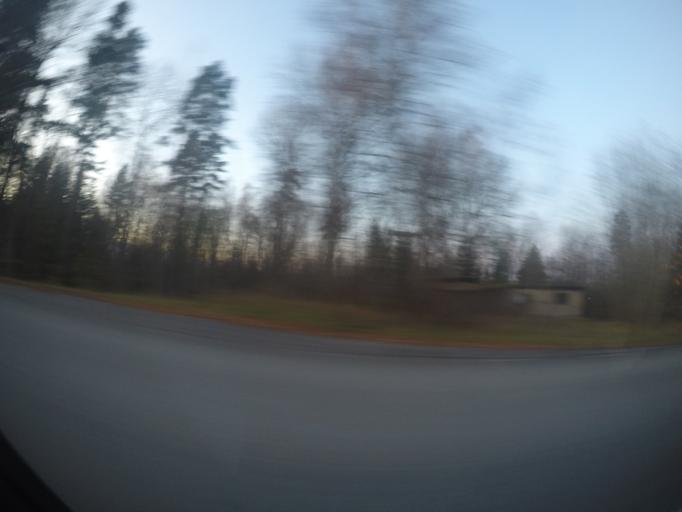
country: SE
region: OErebro
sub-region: Lindesbergs Kommun
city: Frovi
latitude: 59.3220
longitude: 15.4196
